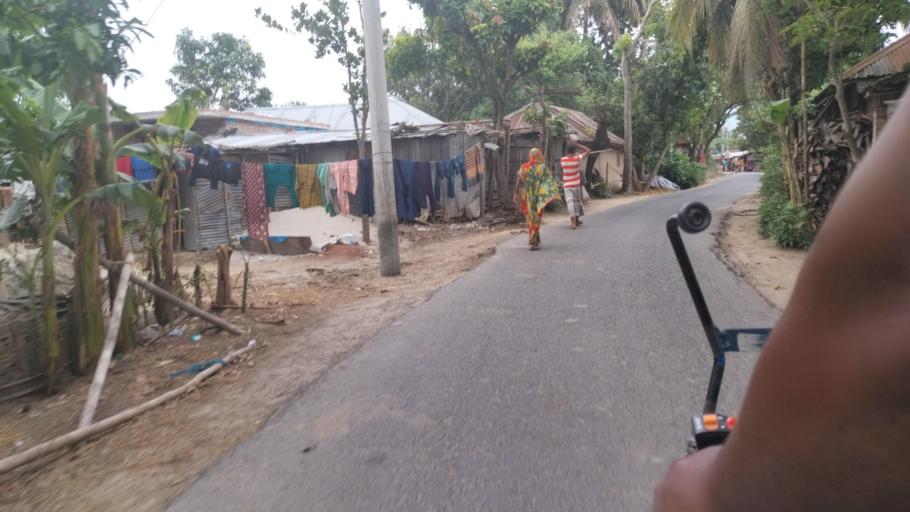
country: BD
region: Rajshahi
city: Rajshahi
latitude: 24.5446
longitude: 88.6283
